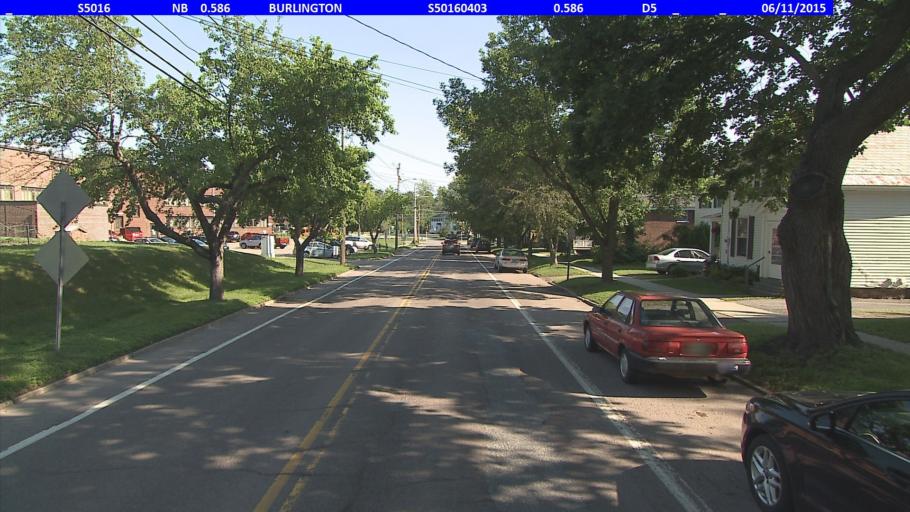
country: US
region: Vermont
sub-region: Chittenden County
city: Winooski
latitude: 44.4810
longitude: -73.1923
